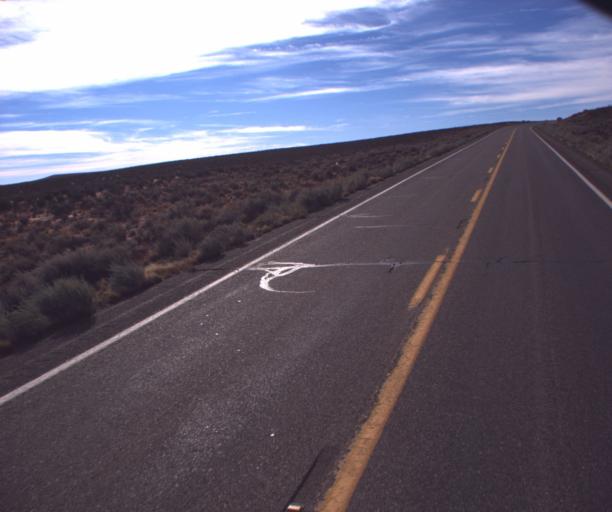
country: US
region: Arizona
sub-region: Coconino County
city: LeChee
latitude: 36.8161
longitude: -111.3066
